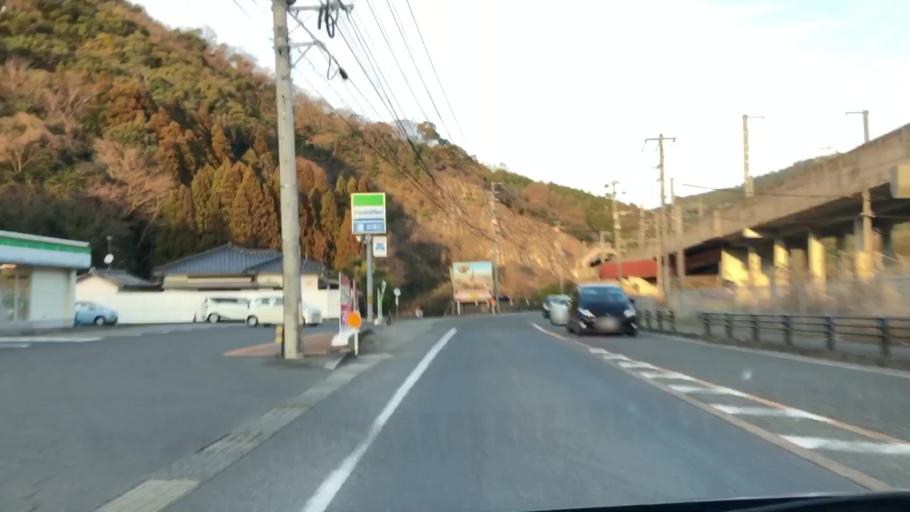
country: JP
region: Kumamoto
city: Minamata
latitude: 32.2132
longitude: 130.4315
